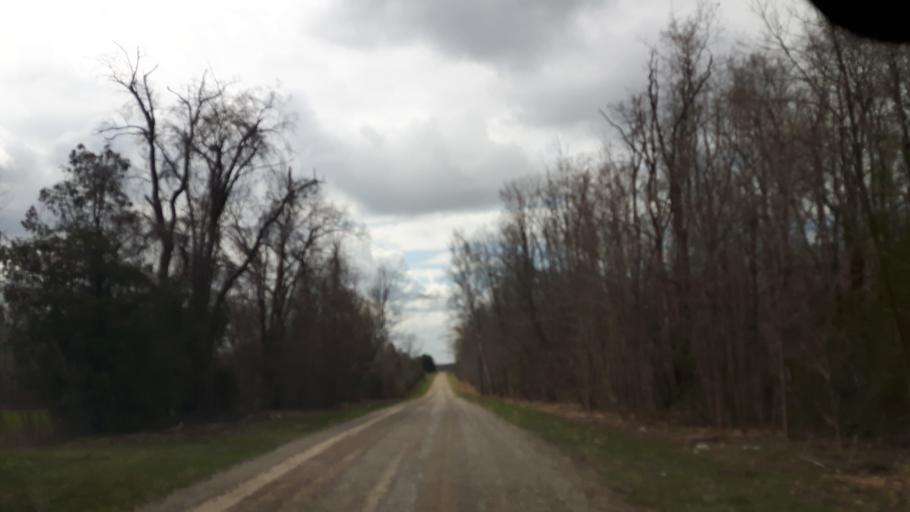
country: CA
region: Ontario
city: Bluewater
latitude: 43.5523
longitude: -81.6801
